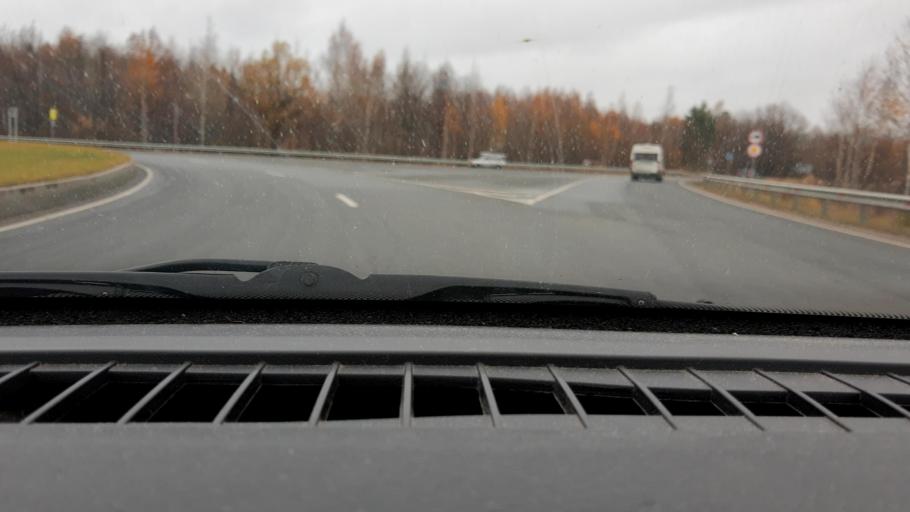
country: RU
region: Nizjnij Novgorod
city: Kstovo
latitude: 56.1251
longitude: 44.1656
